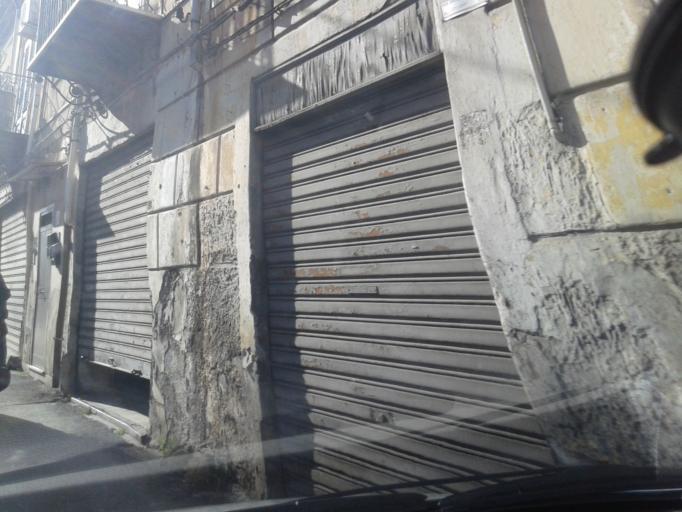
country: IT
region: Sicily
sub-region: Palermo
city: Palermo
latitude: 38.1134
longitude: 13.3423
